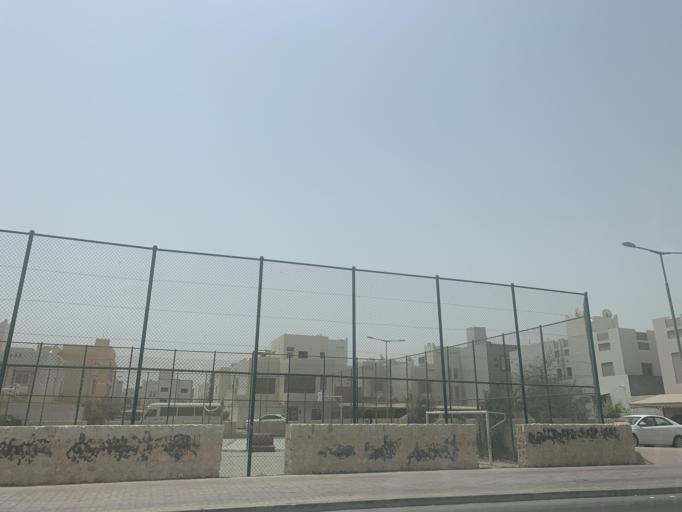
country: BH
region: Manama
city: Jidd Hafs
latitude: 26.2118
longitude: 50.5364
